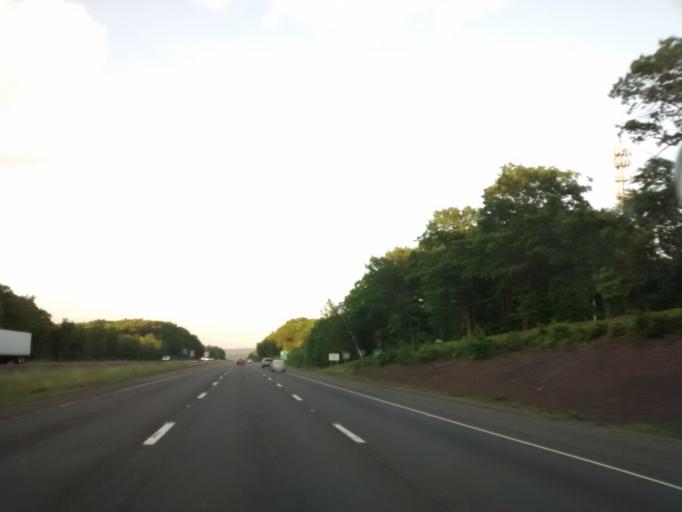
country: US
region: Connecticut
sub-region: Tolland County
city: Tolland
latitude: 41.8733
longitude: -72.3400
